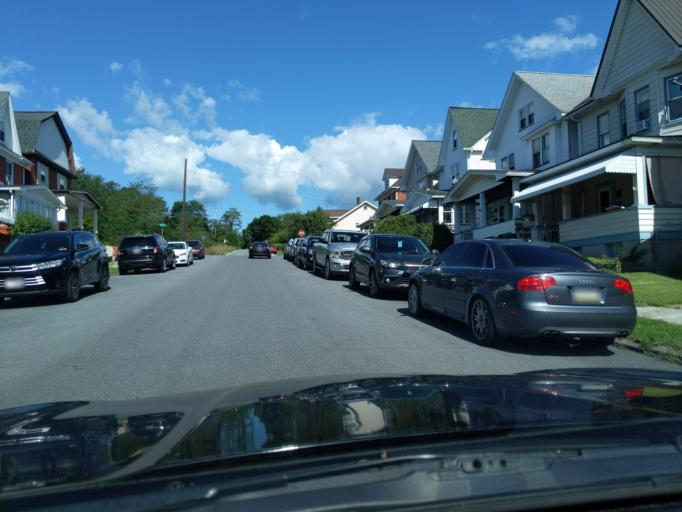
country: US
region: Pennsylvania
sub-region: Blair County
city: Altoona
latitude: 40.5378
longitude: -78.3915
